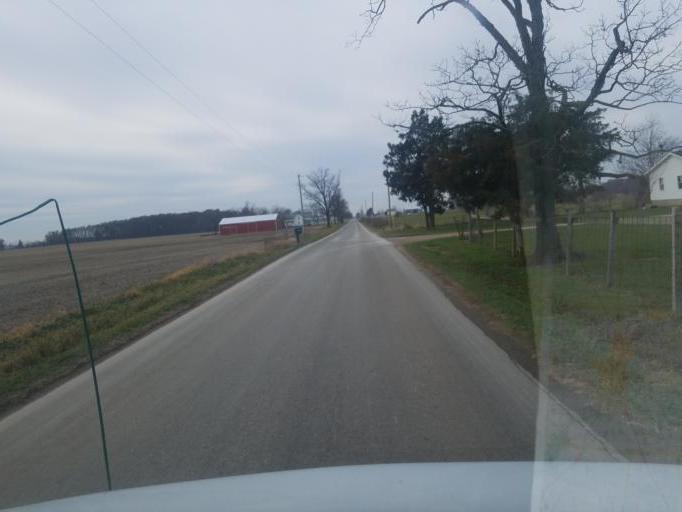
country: US
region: Indiana
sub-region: Adams County
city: Geneva
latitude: 40.6151
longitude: -84.8789
